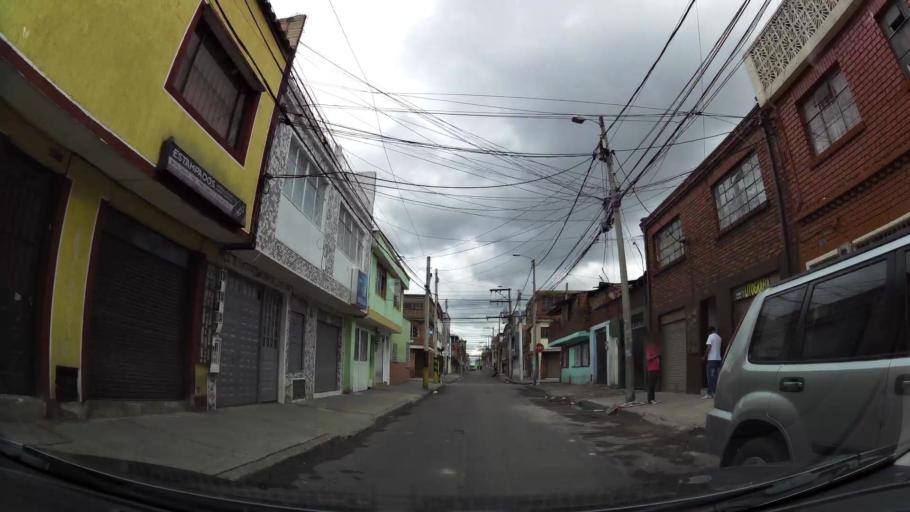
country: CO
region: Bogota D.C.
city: Barrio San Luis
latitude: 4.6811
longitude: -74.0902
